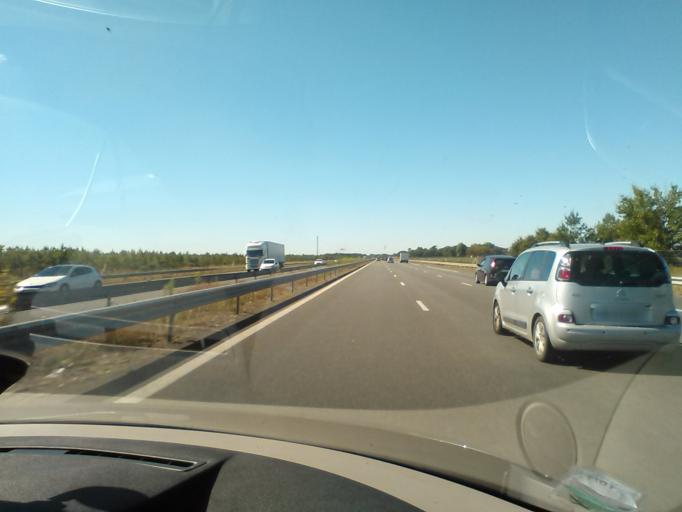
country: FR
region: Aquitaine
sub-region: Departement des Landes
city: Labouheyre
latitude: 44.2477
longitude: -0.9051
